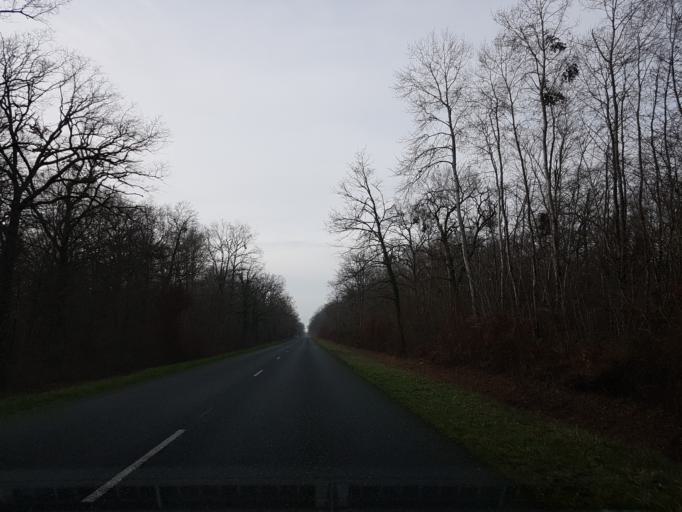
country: FR
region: Auvergne
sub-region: Departement de l'Allier
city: Beaulon
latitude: 46.6261
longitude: 3.5991
